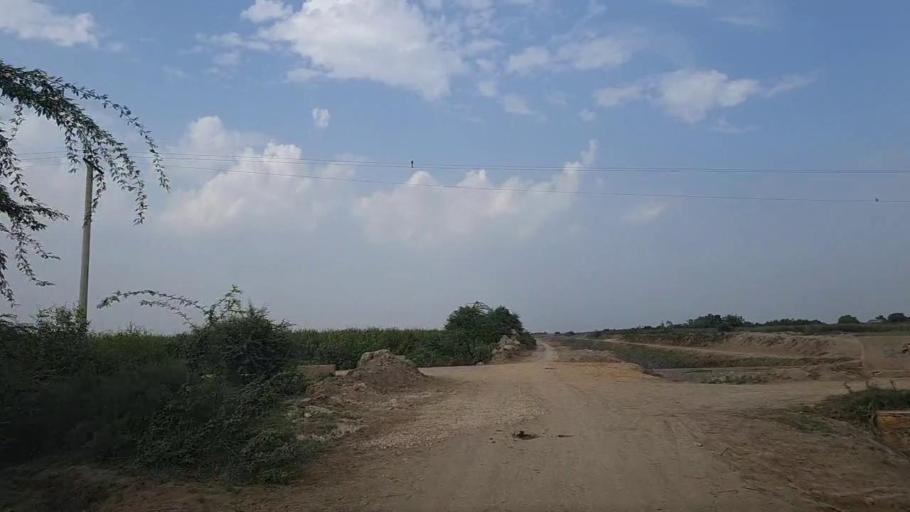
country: PK
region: Sindh
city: Daro Mehar
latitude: 24.7204
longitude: 68.1383
